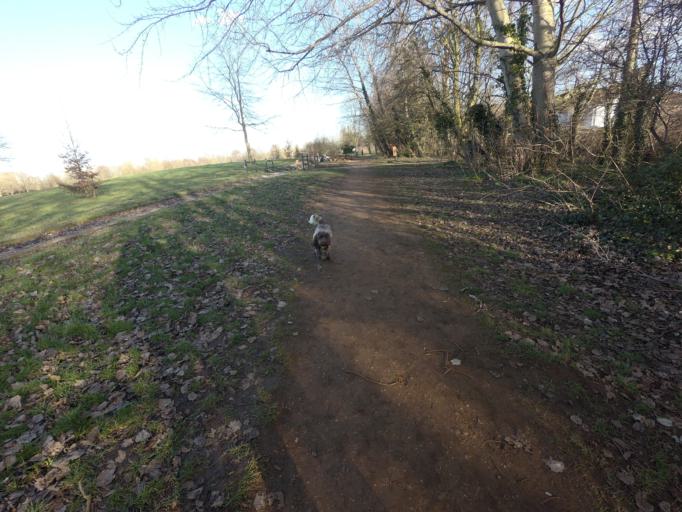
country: GB
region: England
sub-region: Kent
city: Swanley
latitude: 51.4049
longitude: 0.1724
